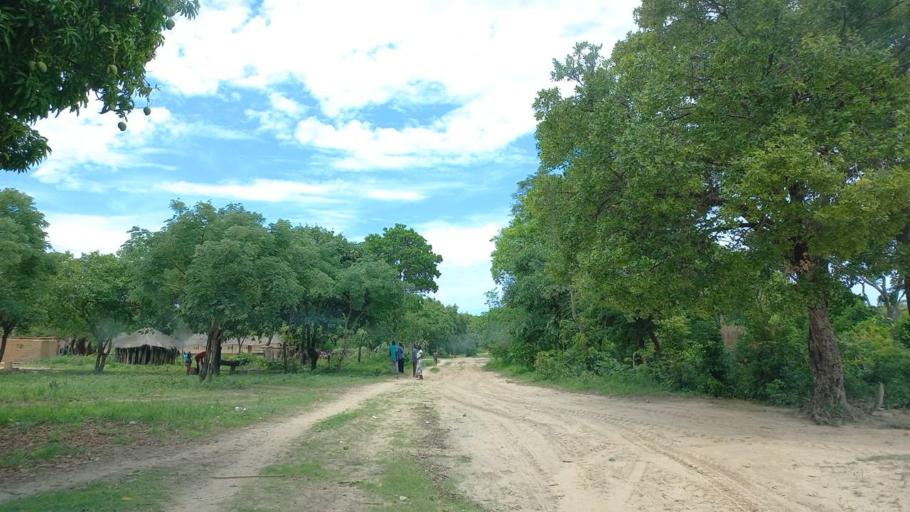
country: ZM
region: North-Western
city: Kabompo
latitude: -13.6177
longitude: 24.2160
